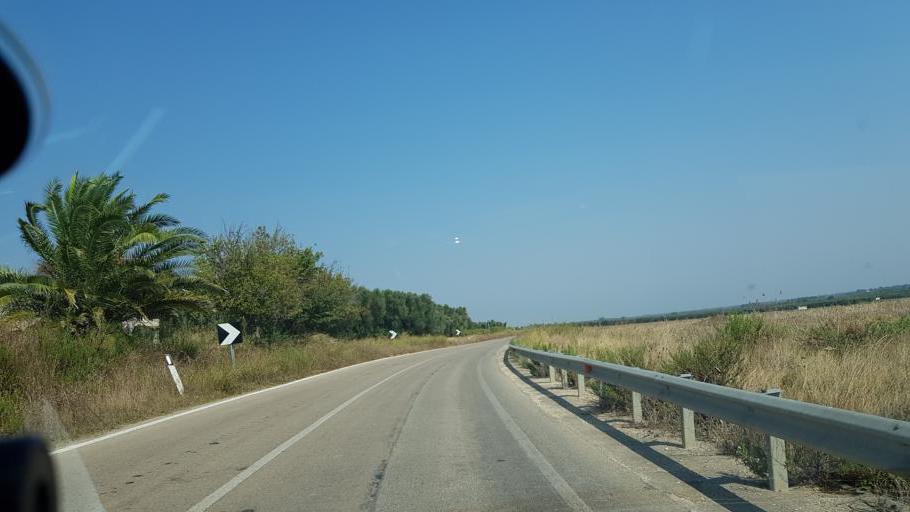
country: IT
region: Apulia
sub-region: Provincia di Brindisi
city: Torre Santa Susanna
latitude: 40.4985
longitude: 17.7220
